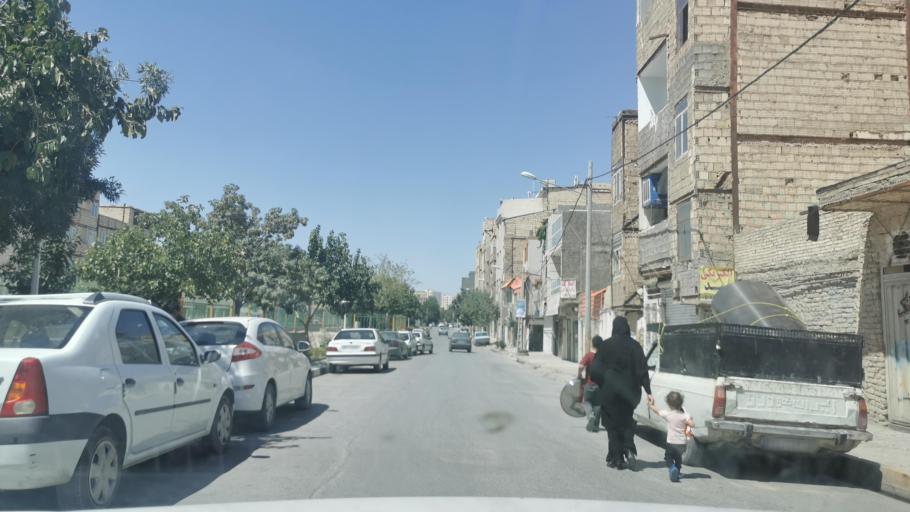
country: IR
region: Razavi Khorasan
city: Mashhad
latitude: 36.3600
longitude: 59.5604
